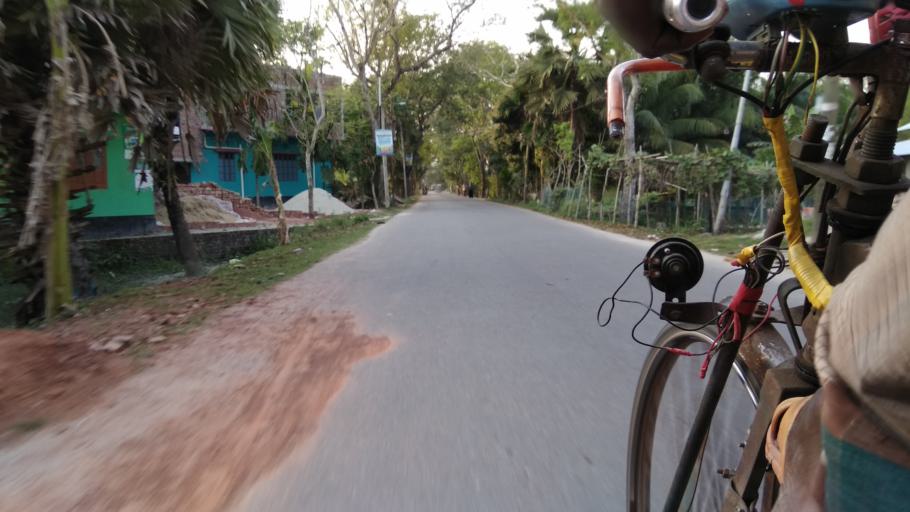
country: BD
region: Barisal
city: Mehendiganj
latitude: 22.9185
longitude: 90.4100
